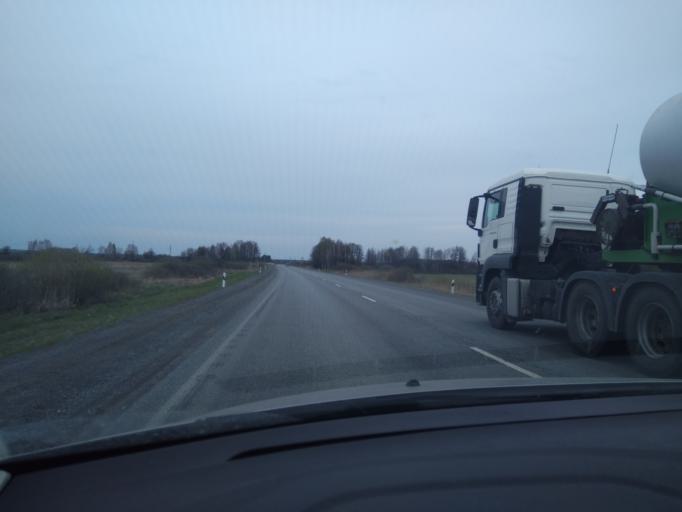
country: RU
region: Sverdlovsk
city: Pyshma
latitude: 57.0217
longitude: 63.3949
